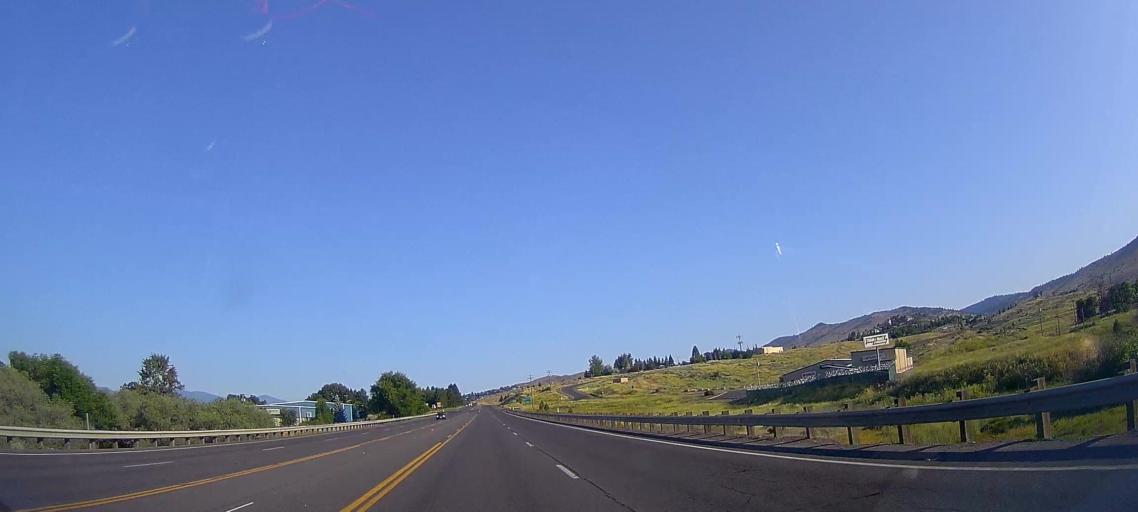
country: US
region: Oregon
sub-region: Klamath County
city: Altamont
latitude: 42.2154
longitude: -121.7452
